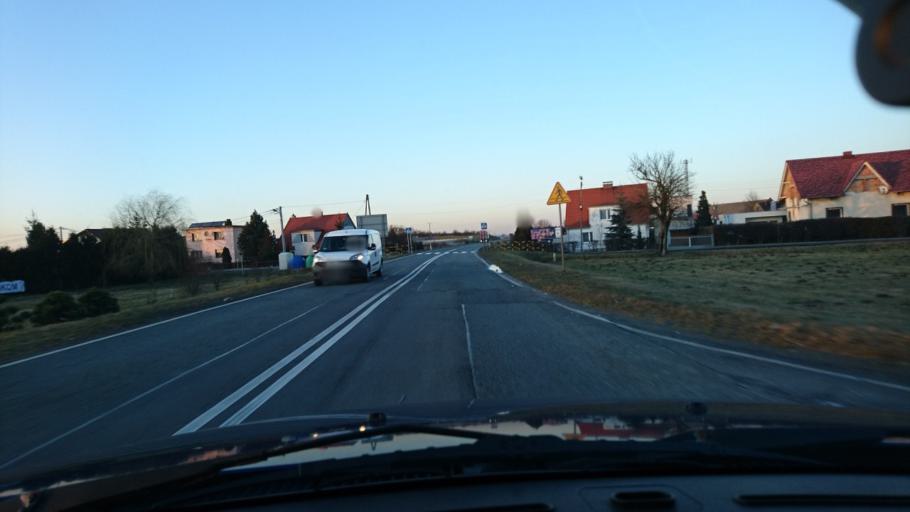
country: PL
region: Silesian Voivodeship
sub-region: Powiat gliwicki
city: Wielowies
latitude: 50.5041
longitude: 18.6046
